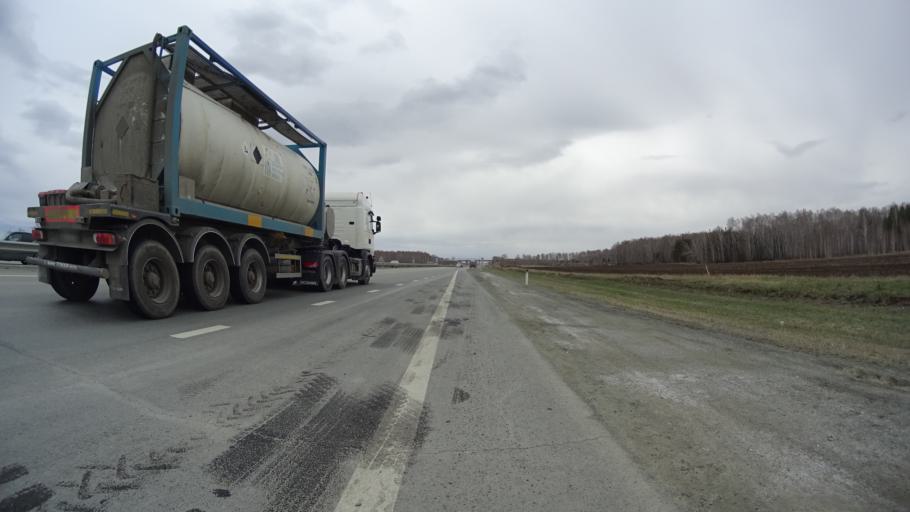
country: RU
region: Chelyabinsk
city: Yemanzhelinka
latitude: 54.8217
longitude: 61.3090
